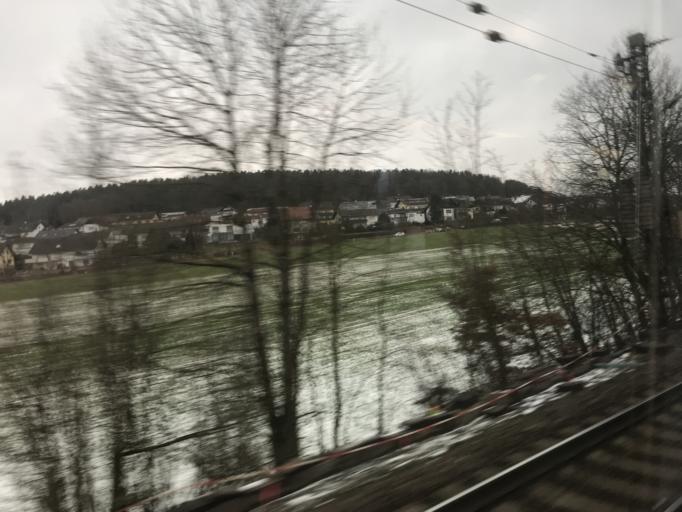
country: DE
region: Hesse
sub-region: Regierungsbezirk Kassel
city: Petersberg
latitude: 50.5816
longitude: 9.7248
